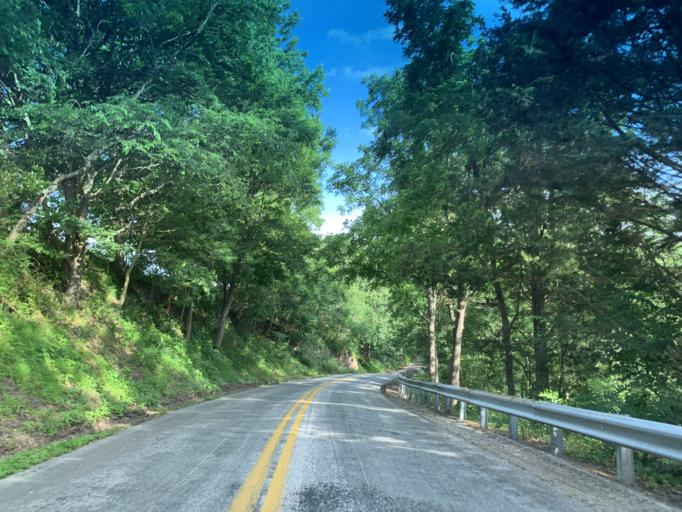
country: US
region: Pennsylvania
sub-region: York County
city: Stewartstown
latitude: 39.7511
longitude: -76.5409
